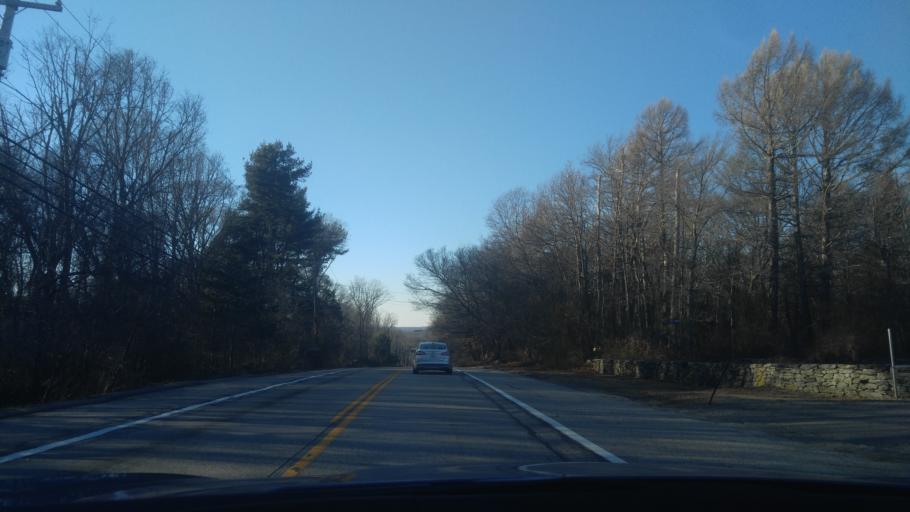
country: US
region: Rhode Island
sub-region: Washington County
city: North Kingstown
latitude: 41.5330
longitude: -71.4312
